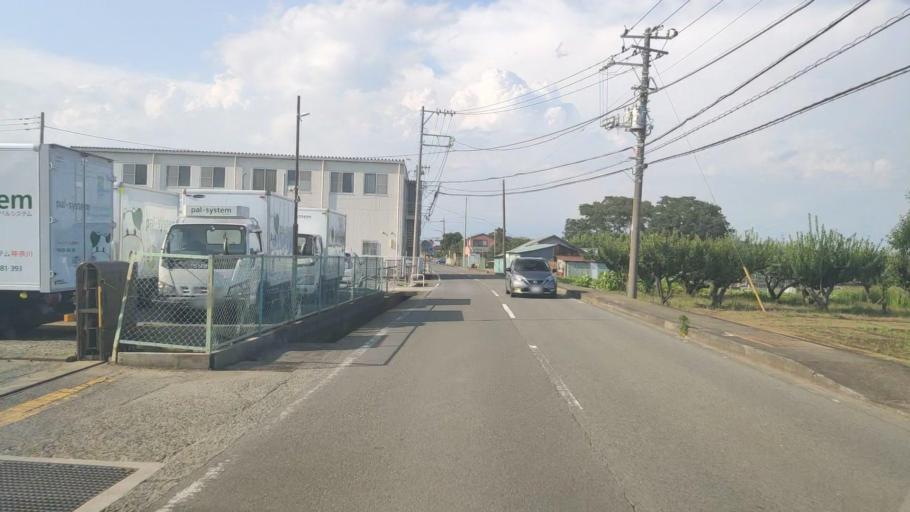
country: JP
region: Kanagawa
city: Isehara
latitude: 35.3814
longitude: 139.3381
